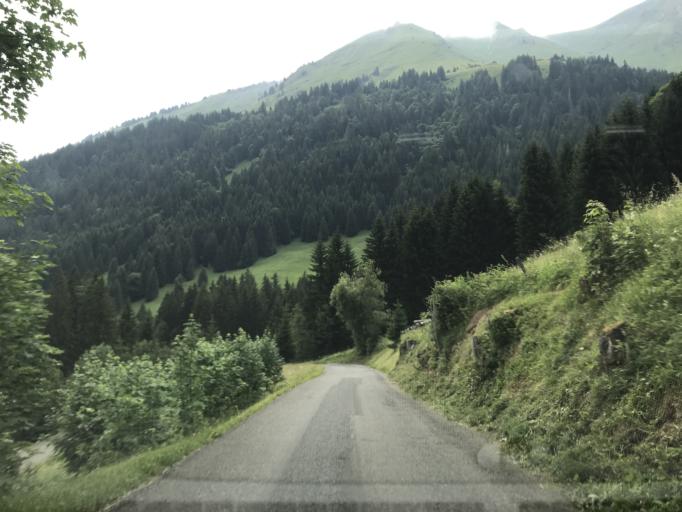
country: FR
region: Rhone-Alpes
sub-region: Departement de la Haute-Savoie
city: Morzine
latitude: 46.1481
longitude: 6.7601
